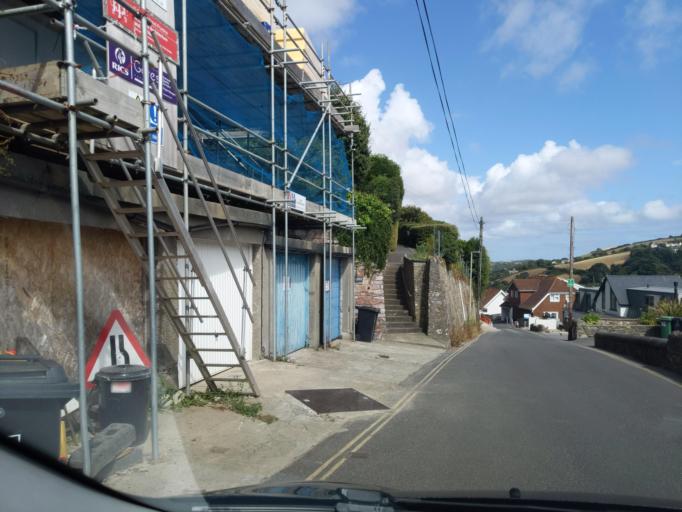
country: GB
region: England
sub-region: Devon
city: Salcombe
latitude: 50.2333
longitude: -3.7726
